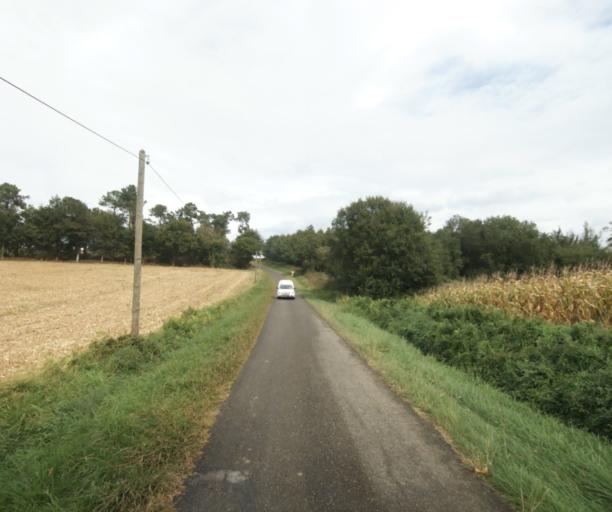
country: FR
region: Midi-Pyrenees
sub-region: Departement du Gers
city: Cazaubon
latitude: 43.9012
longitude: -0.1326
